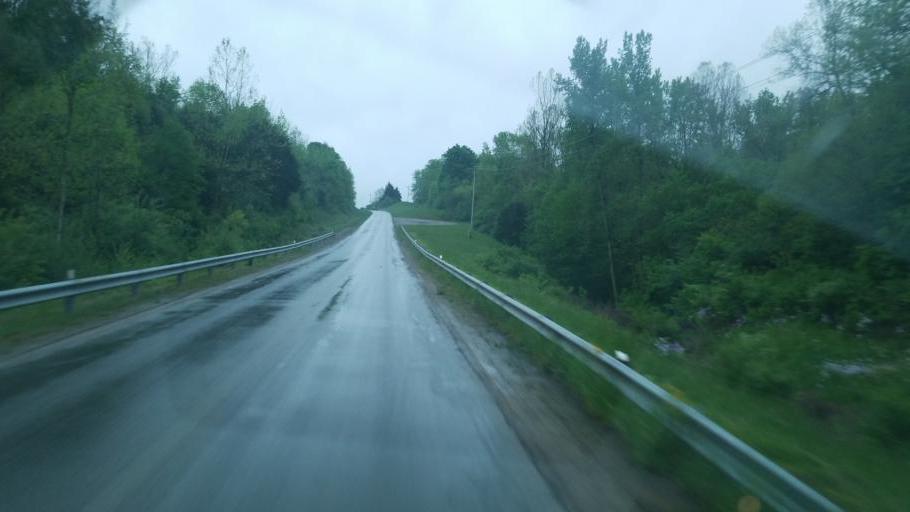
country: US
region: Ohio
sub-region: Highland County
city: Greenfield
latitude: 39.2929
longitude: -83.4623
